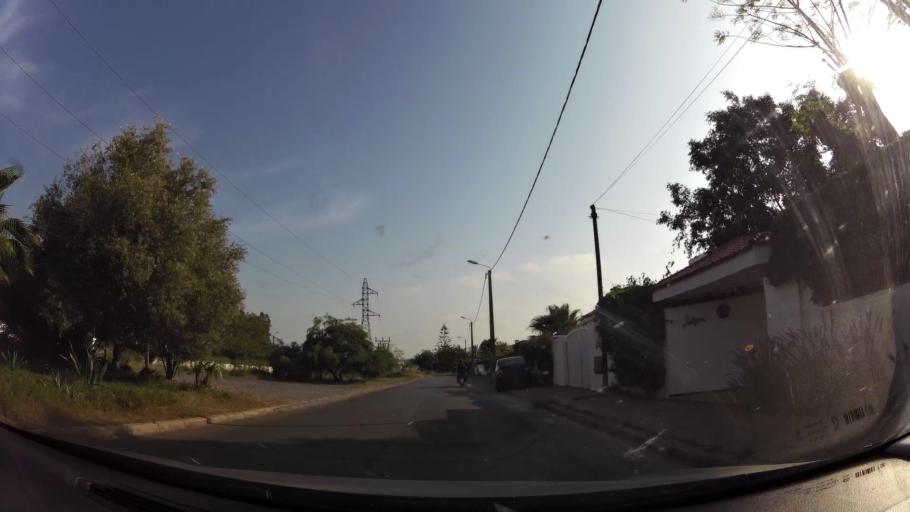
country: MA
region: Rabat-Sale-Zemmour-Zaer
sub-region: Rabat
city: Rabat
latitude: 33.9346
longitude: -6.8116
